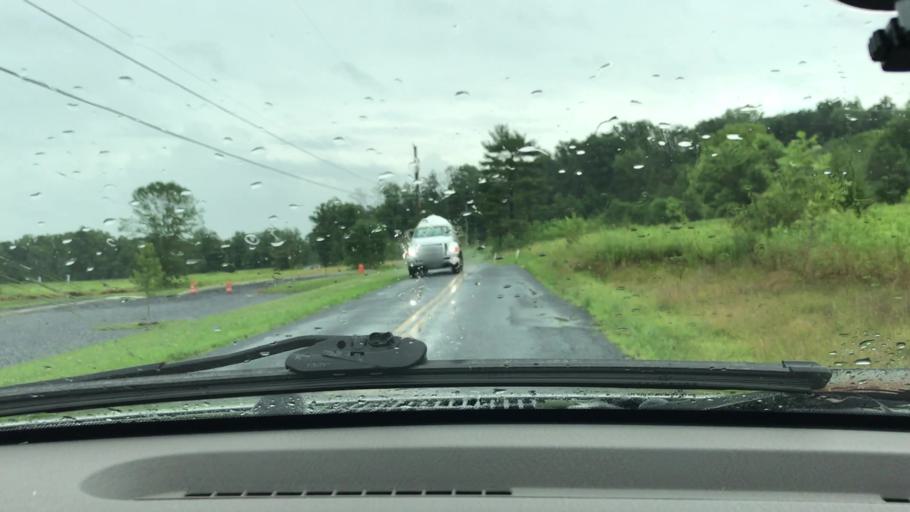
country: US
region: Pennsylvania
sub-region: Lancaster County
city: Elizabethtown
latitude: 40.1852
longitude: -76.5974
